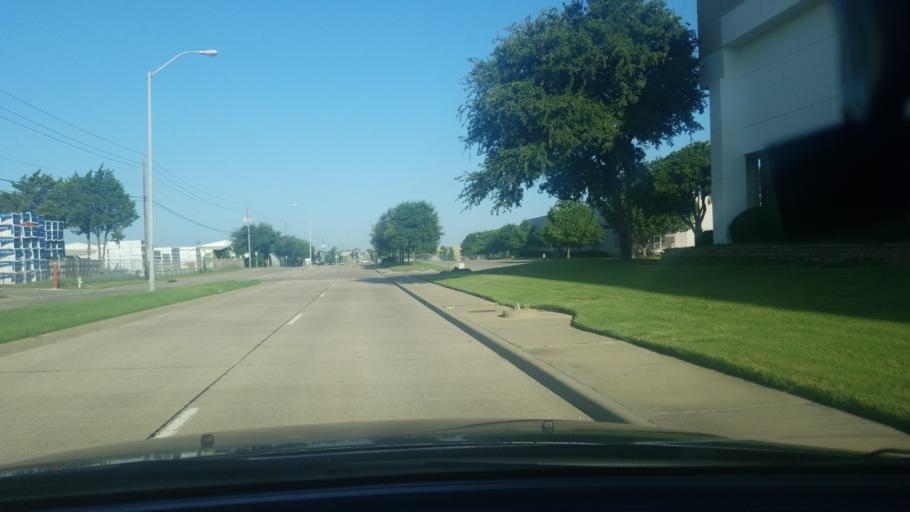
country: US
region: Texas
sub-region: Dallas County
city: Balch Springs
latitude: 32.7780
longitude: -96.6690
